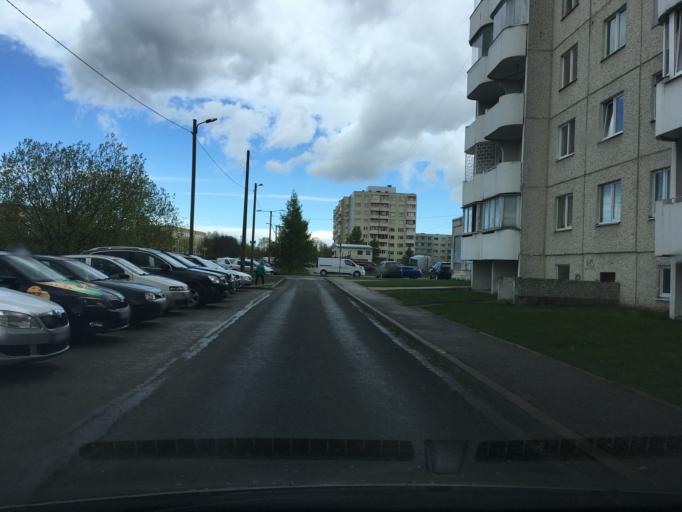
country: EE
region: Harju
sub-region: Tallinna linn
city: Kose
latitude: 59.4485
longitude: 24.8465
